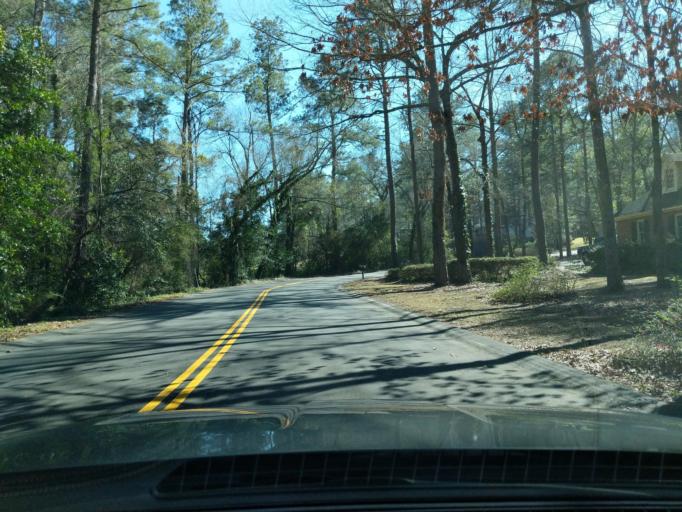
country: US
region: South Carolina
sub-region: Aiken County
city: Aiken
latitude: 33.5328
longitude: -81.7445
